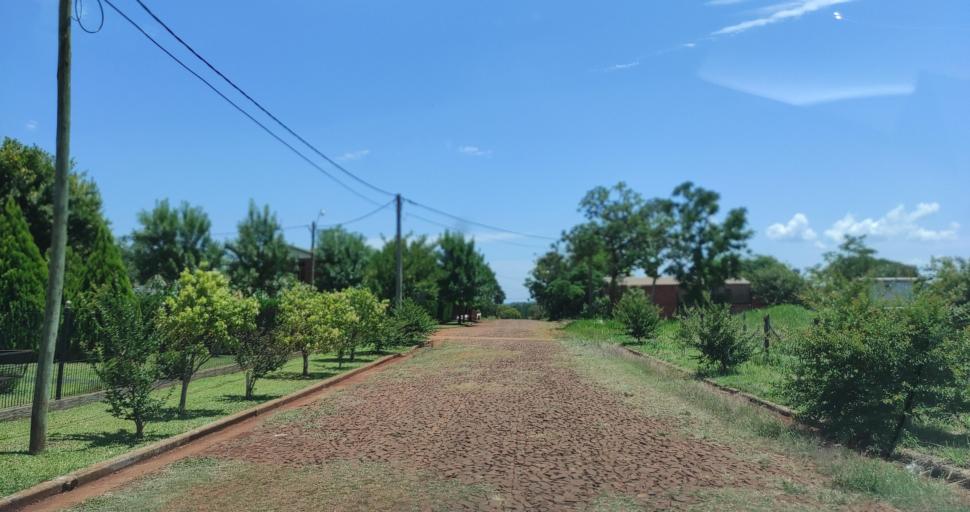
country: AR
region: Misiones
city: Ruiz de Montoya
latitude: -26.9724
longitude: -55.0486
